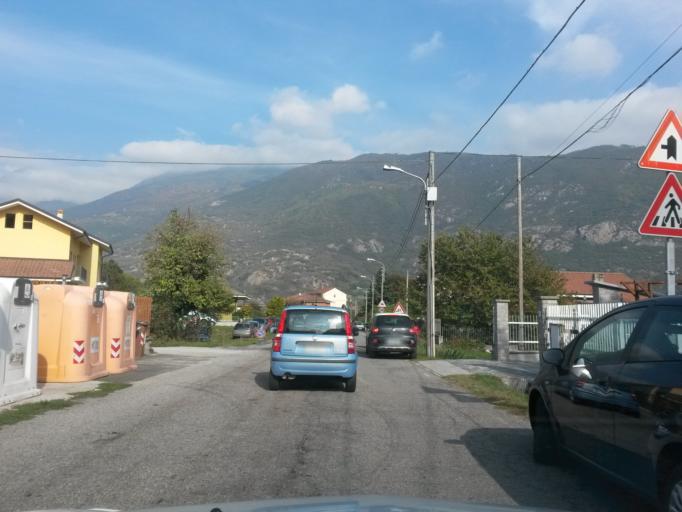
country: IT
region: Piedmont
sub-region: Provincia di Torino
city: Baratte
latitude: 45.1123
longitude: 7.2346
